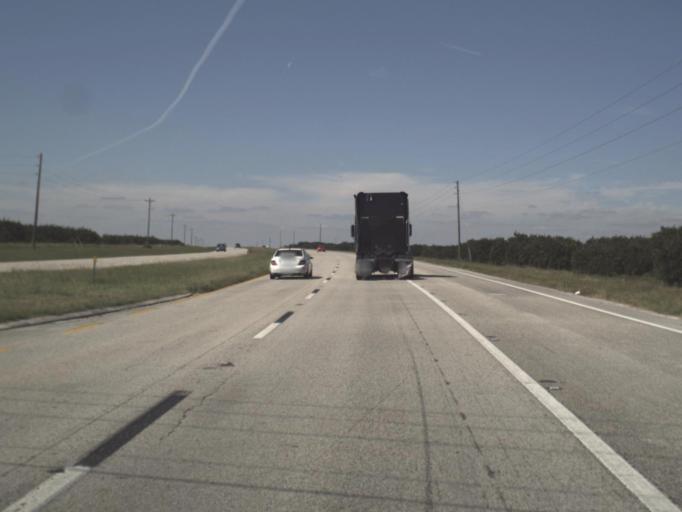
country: US
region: Florida
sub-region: Highlands County
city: Lake Placid
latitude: 27.3549
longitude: -81.3889
